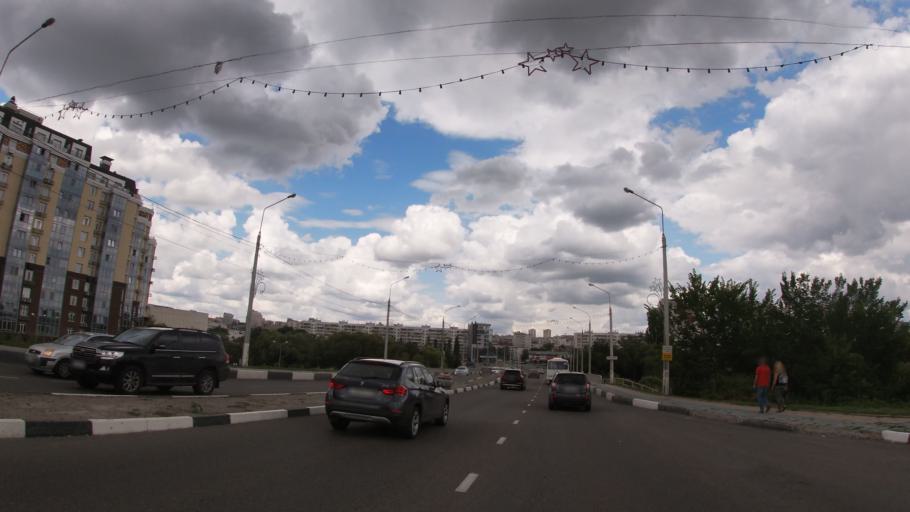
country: RU
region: Belgorod
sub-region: Belgorodskiy Rayon
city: Belgorod
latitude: 50.5888
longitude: 36.5892
